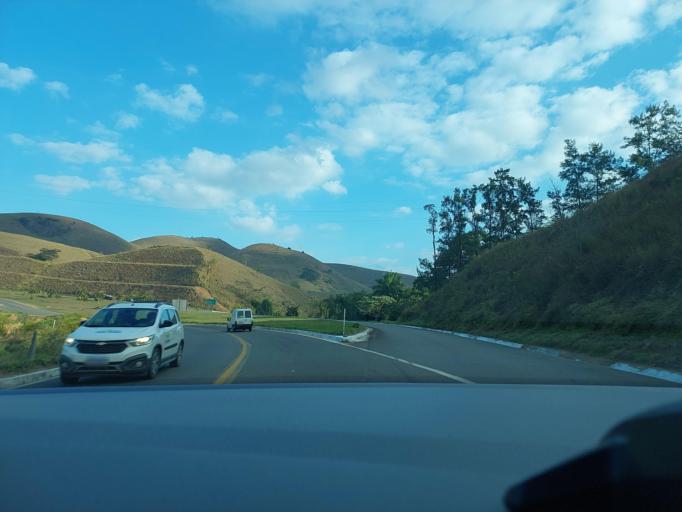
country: BR
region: Minas Gerais
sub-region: Muriae
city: Muriae
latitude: -21.0720
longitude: -42.5071
